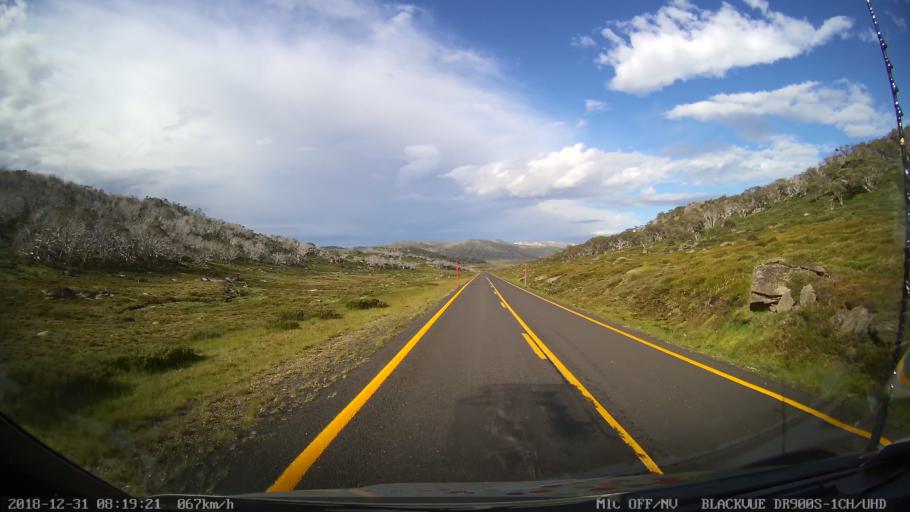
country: AU
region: New South Wales
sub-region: Snowy River
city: Jindabyne
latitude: -36.4188
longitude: 148.3868
